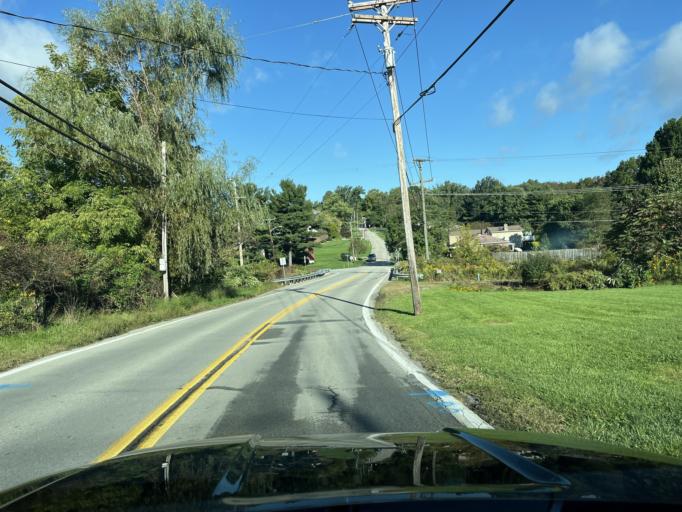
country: US
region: Pennsylvania
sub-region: Fayette County
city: South Uniontown
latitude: 39.8829
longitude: -79.7515
